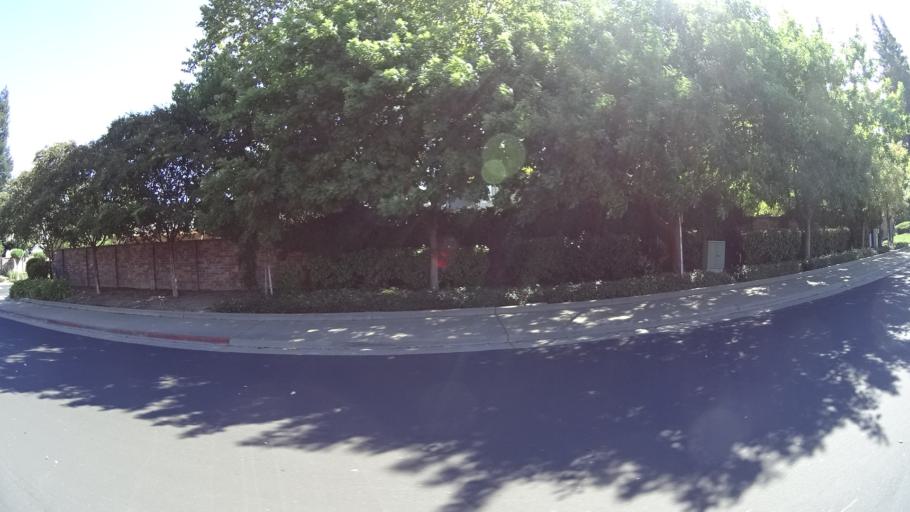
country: US
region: California
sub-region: Sacramento County
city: Laguna
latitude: 38.4242
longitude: -121.4310
